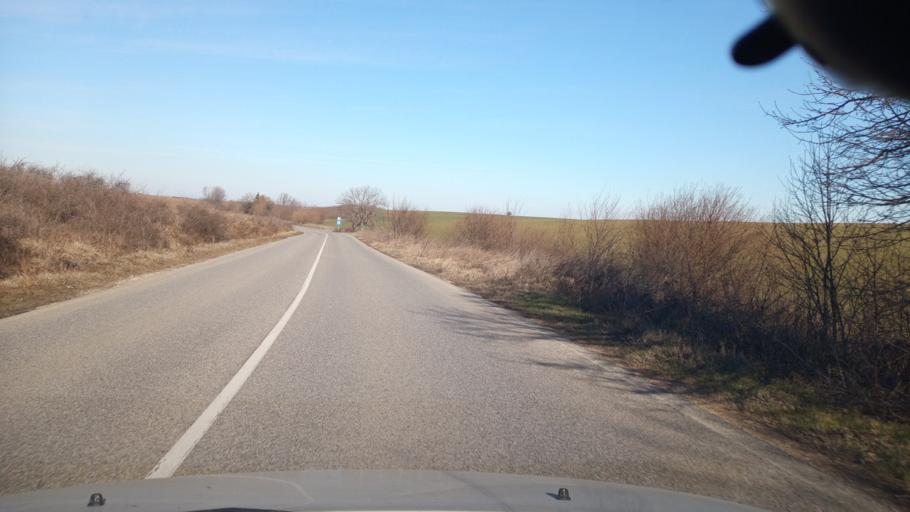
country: BG
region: Pleven
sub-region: Obshtina Pleven
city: Pleven
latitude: 43.4491
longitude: 24.7260
